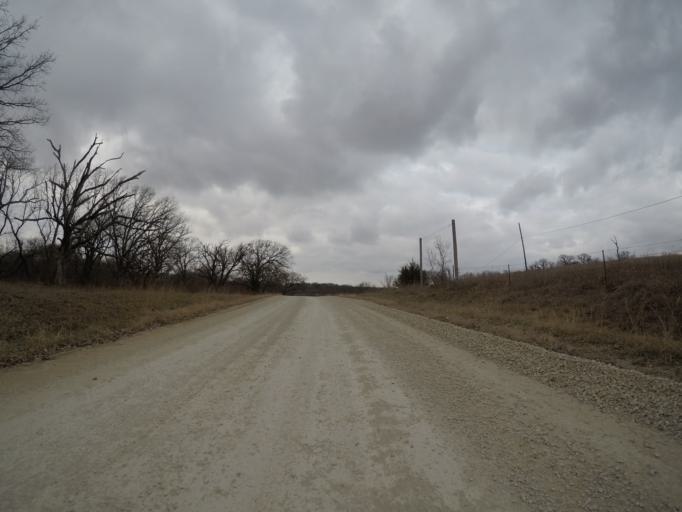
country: US
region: Kansas
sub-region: Morris County
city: Council Grove
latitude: 38.7640
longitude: -96.2798
